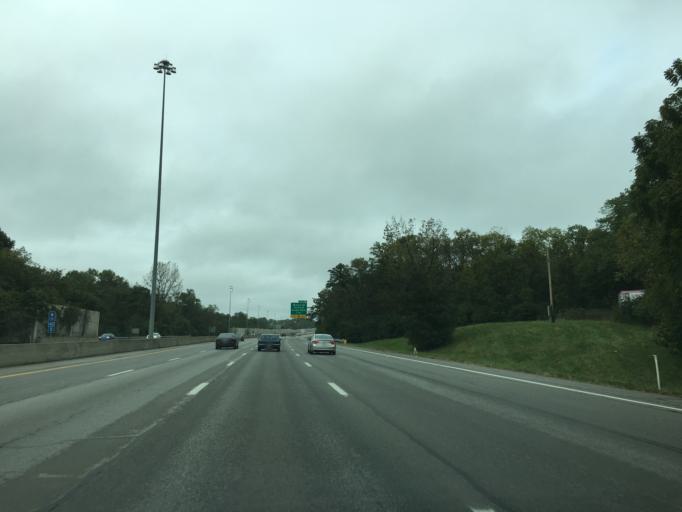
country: US
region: Ohio
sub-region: Hamilton County
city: Forest Park
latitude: 39.2960
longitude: -84.4937
